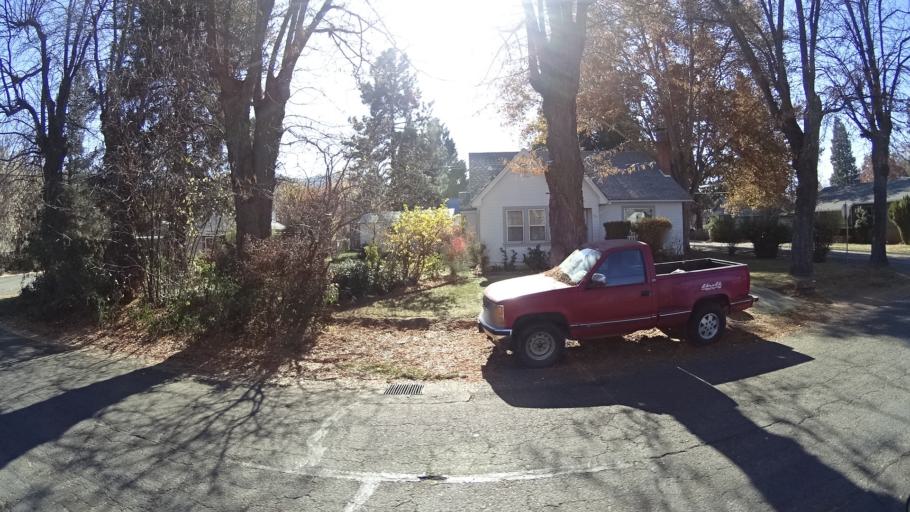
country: US
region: California
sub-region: Siskiyou County
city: Yreka
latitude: 41.7357
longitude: -122.6327
